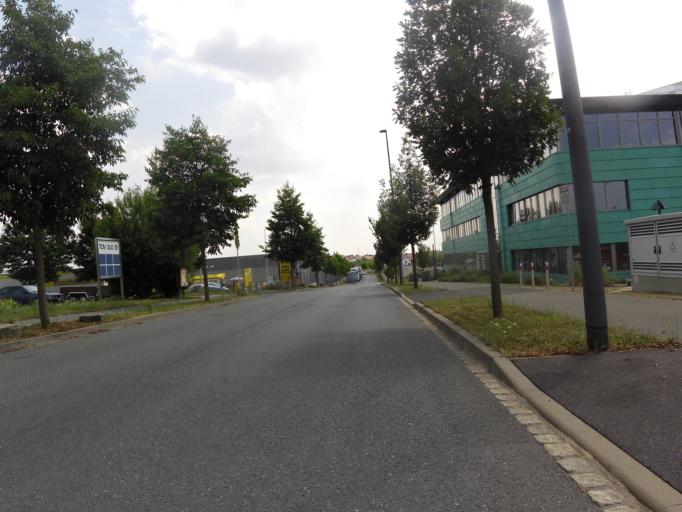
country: DE
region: Bavaria
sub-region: Regierungsbezirk Unterfranken
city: Randersacker
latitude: 49.7303
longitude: 9.9589
